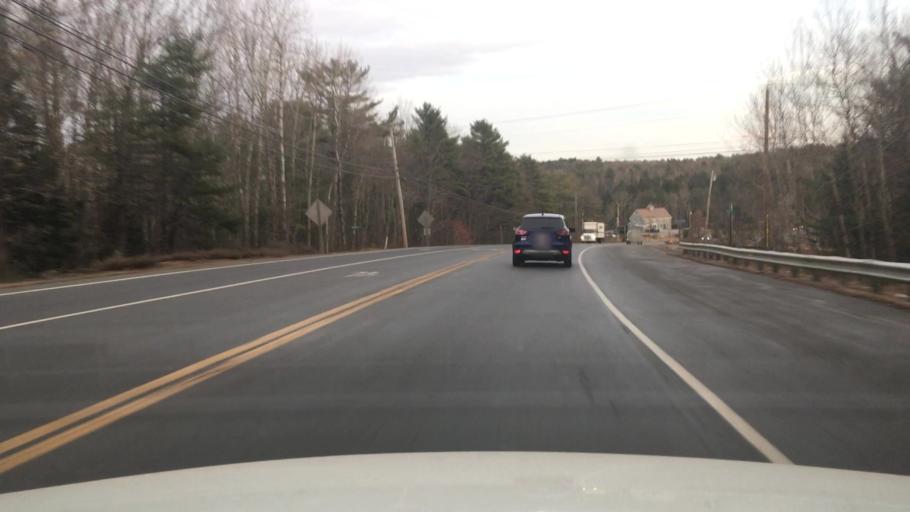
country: US
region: Maine
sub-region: Lincoln County
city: Wiscasset
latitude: 44.0027
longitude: -69.6297
